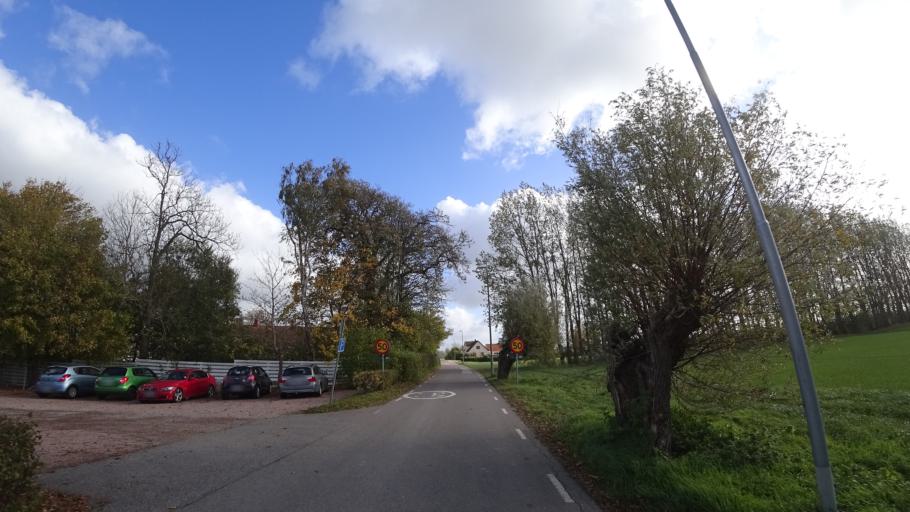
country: SE
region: Skane
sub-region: Staffanstorps Kommun
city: Hjaerup
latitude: 55.6401
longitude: 13.1509
